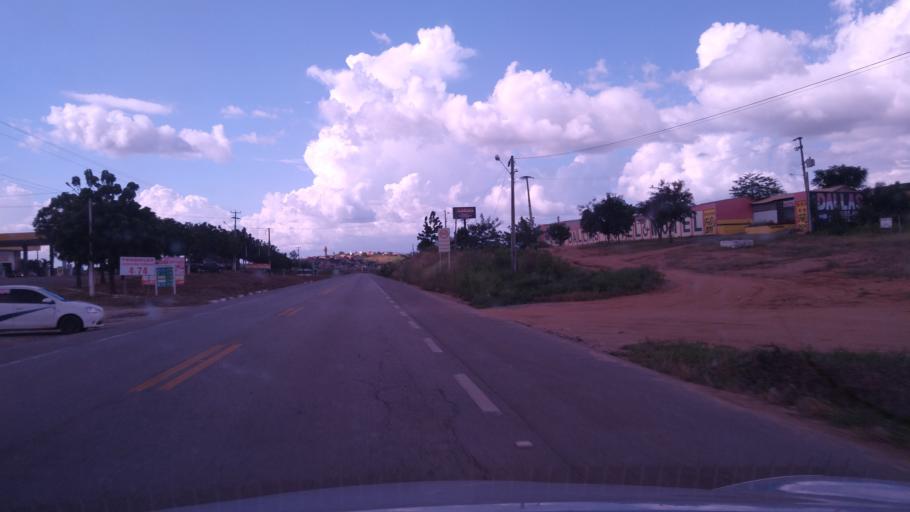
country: BR
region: Ceara
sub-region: Caninde
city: Caninde
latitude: -4.3832
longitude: -39.3111
